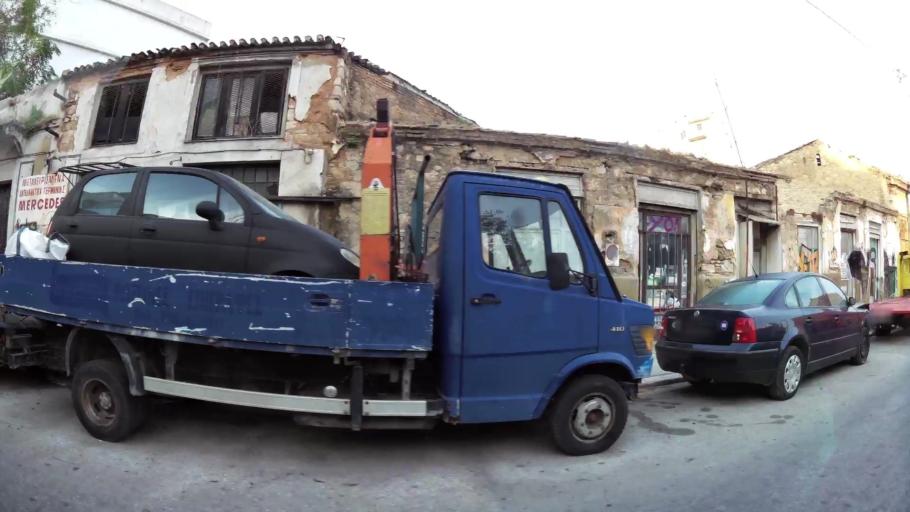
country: GR
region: Attica
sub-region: Nomarchia Athinas
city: Athens
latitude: 37.9855
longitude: 23.7173
